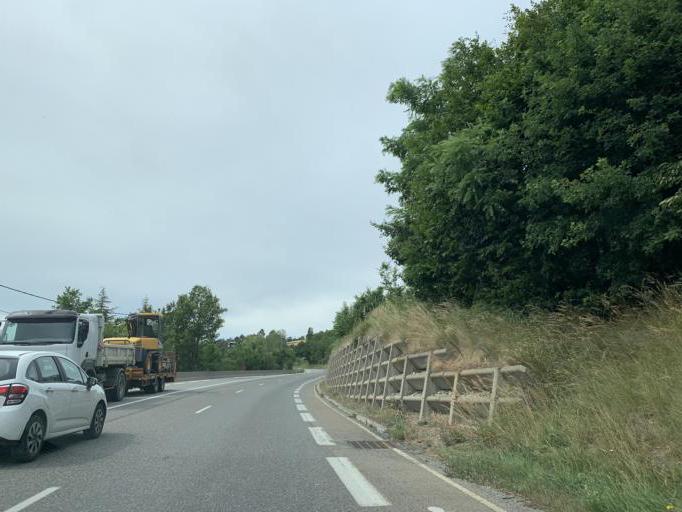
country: FR
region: Provence-Alpes-Cote d'Azur
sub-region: Departement des Hautes-Alpes
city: Gap
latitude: 44.5540
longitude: 6.0405
